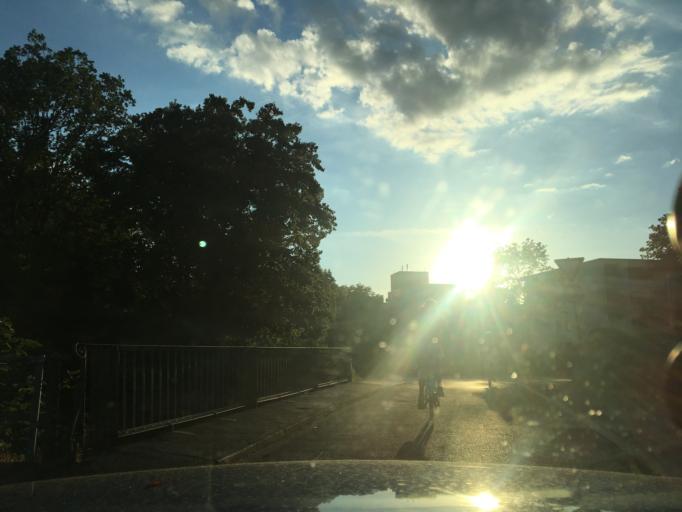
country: DE
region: Hesse
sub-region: Regierungsbezirk Darmstadt
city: Darmstadt
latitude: 49.8858
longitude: 8.6739
